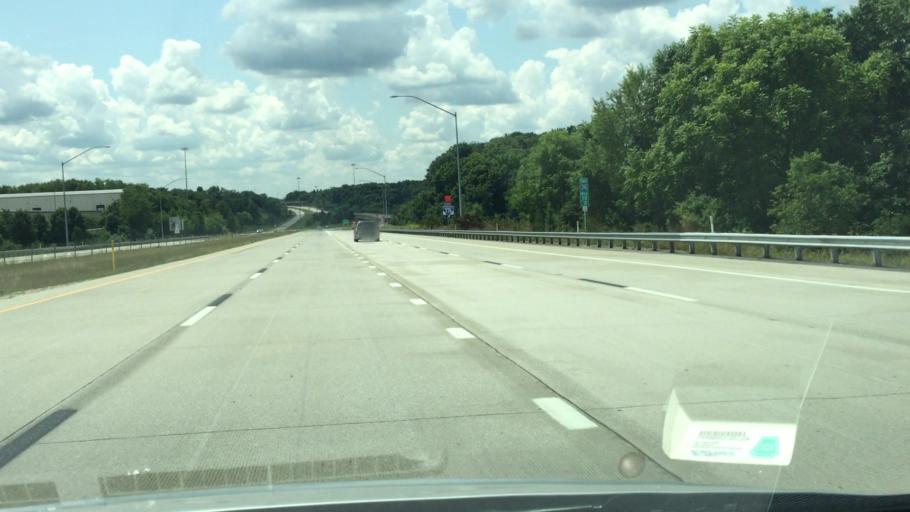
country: US
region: Pennsylvania
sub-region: Allegheny County
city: Carnot-Moon
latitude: 40.5297
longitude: -80.2726
